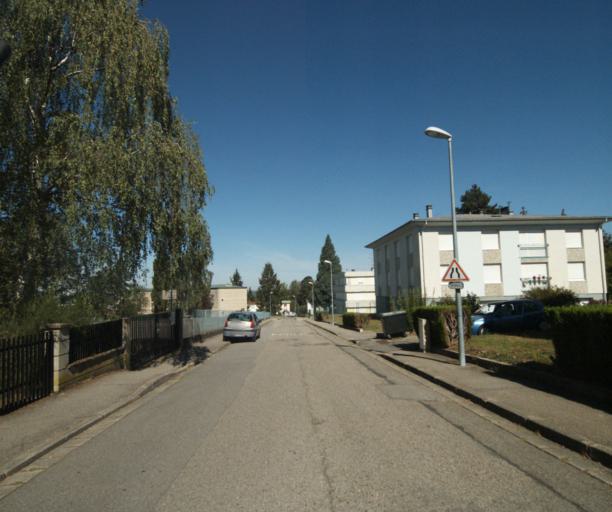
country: FR
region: Lorraine
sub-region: Departement des Vosges
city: Epinal
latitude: 48.1853
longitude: 6.4566
